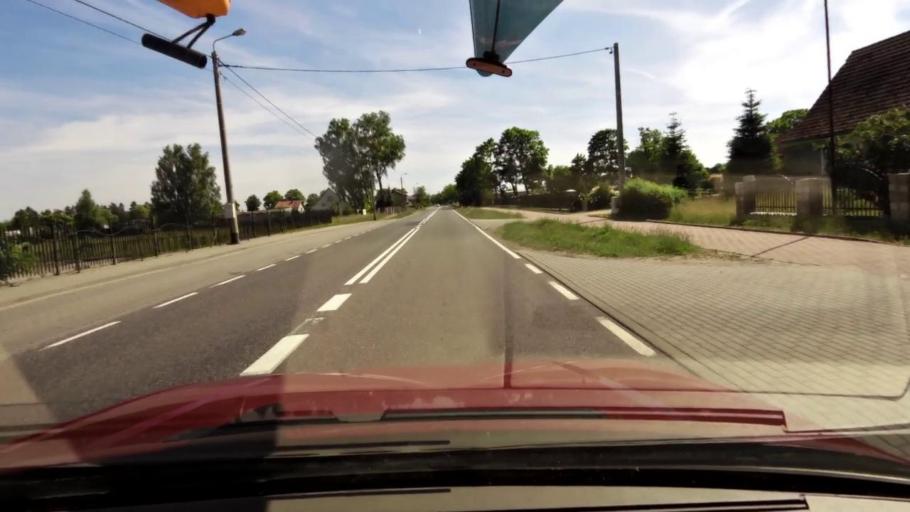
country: PL
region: Pomeranian Voivodeship
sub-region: Powiat slupski
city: Kobylnica
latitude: 54.4137
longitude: 17.0077
